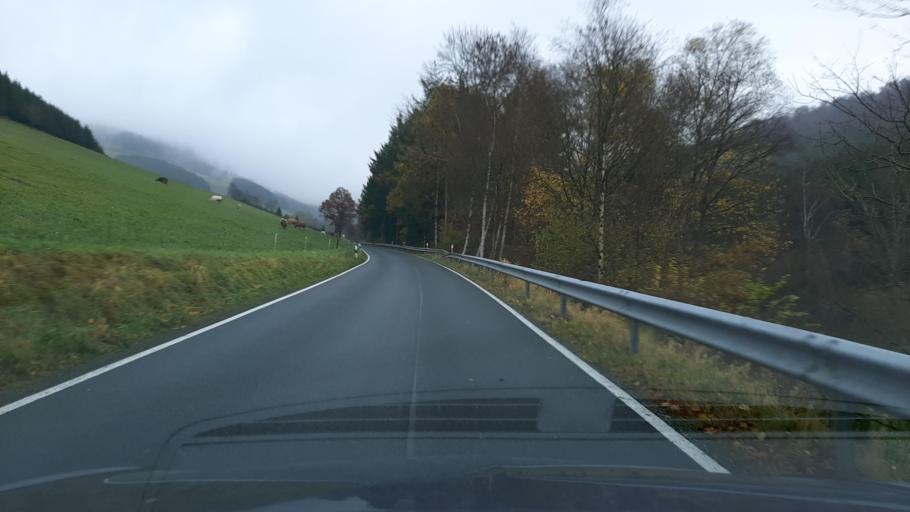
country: DE
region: North Rhine-Westphalia
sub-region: Regierungsbezirk Arnsberg
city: Bad Fredeburg
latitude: 51.1942
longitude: 8.3854
